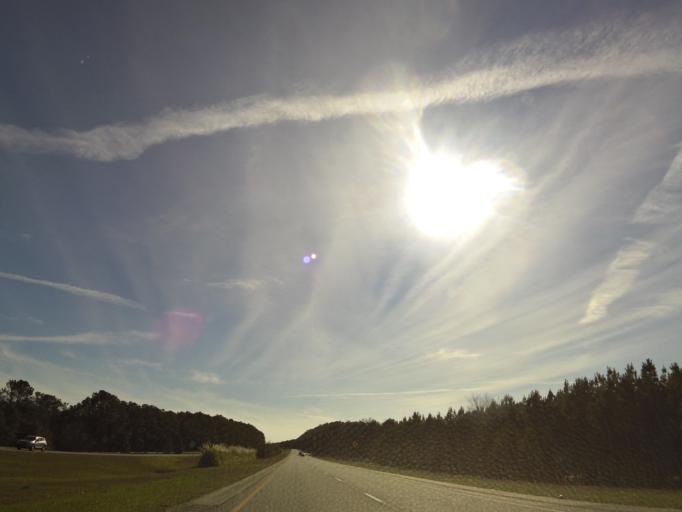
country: US
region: Alabama
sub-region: Russell County
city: Phenix City
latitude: 32.6026
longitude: -84.9528
